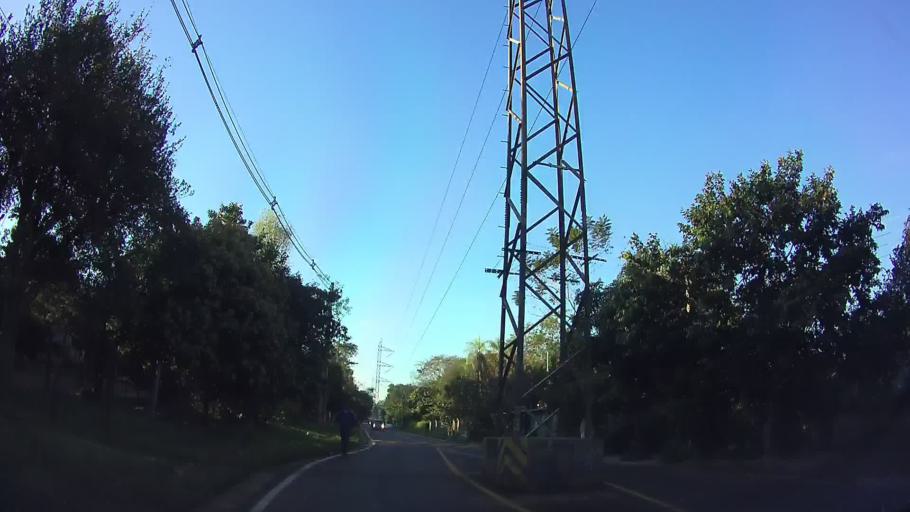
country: PY
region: Central
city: San Lorenzo
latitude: -25.2829
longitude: -57.4664
